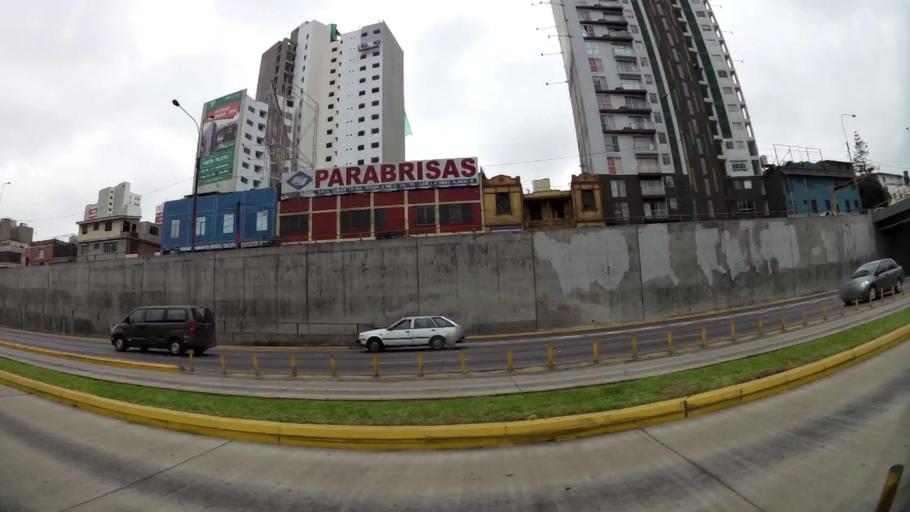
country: PE
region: Lima
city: Lima
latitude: -12.0708
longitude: -77.0314
